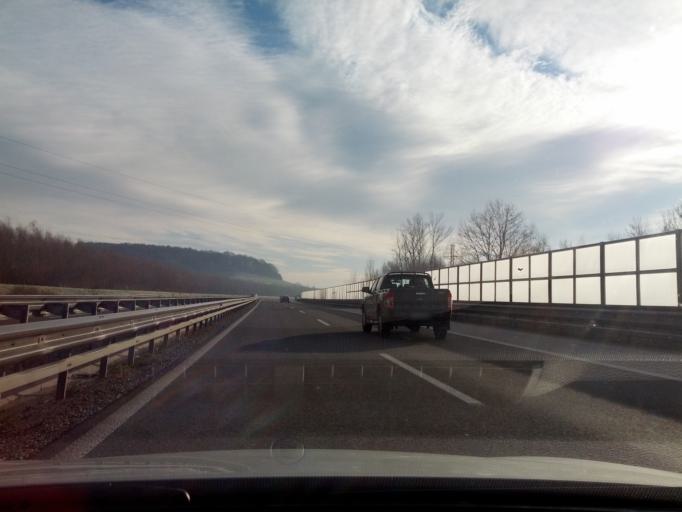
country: SI
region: Pesnica
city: Pesnica pri Mariboru
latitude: 46.5840
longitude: 15.7247
